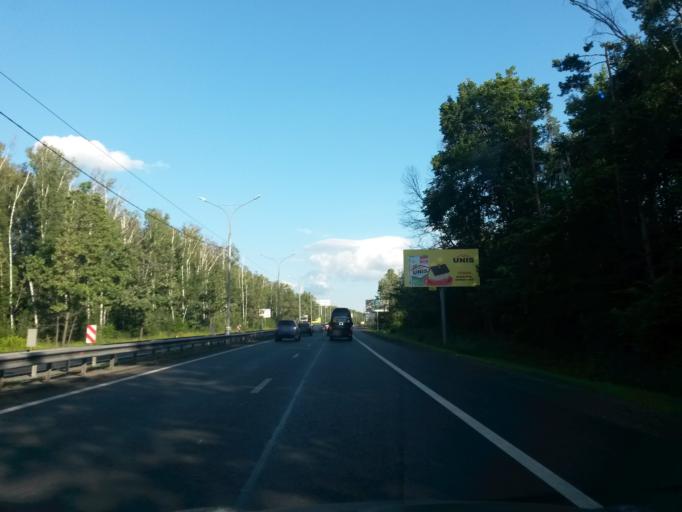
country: RU
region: Moskovskaya
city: Petrovskaya
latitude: 55.5518
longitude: 37.7875
